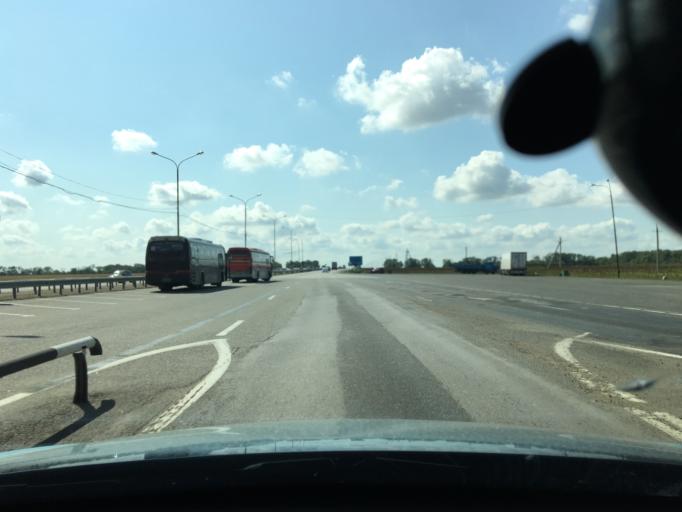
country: RU
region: Krasnodarskiy
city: Krasnoye
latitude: 46.7594
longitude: 39.6609
